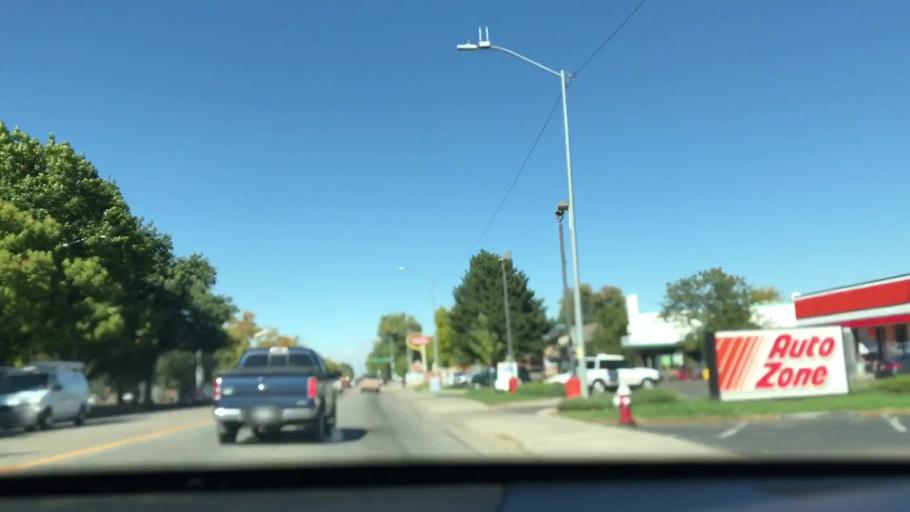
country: US
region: Colorado
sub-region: Boulder County
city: Longmont
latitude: 40.1793
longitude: -105.1023
